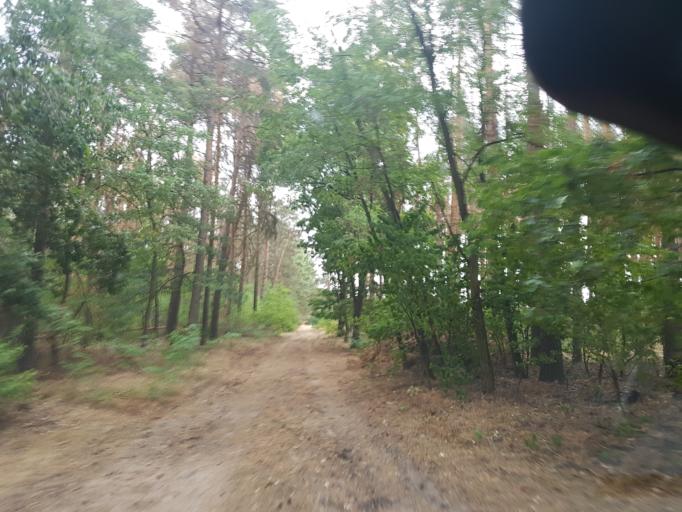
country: DE
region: Brandenburg
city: Schilda
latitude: 51.5701
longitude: 13.3357
